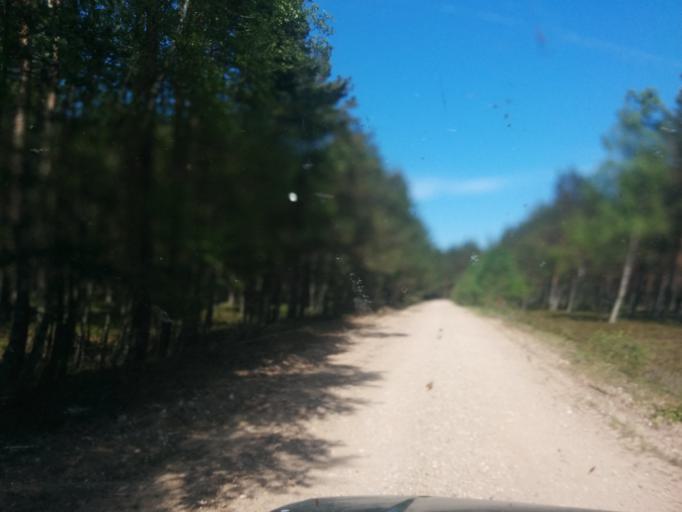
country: LV
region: Dundaga
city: Dundaga
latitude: 57.6219
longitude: 22.0940
